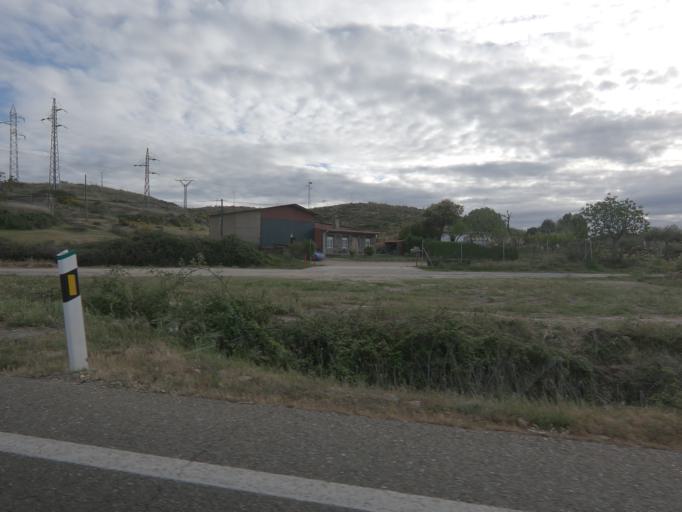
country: ES
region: Extremadura
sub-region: Provincia de Caceres
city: Coria
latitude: 39.9590
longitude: -6.5133
